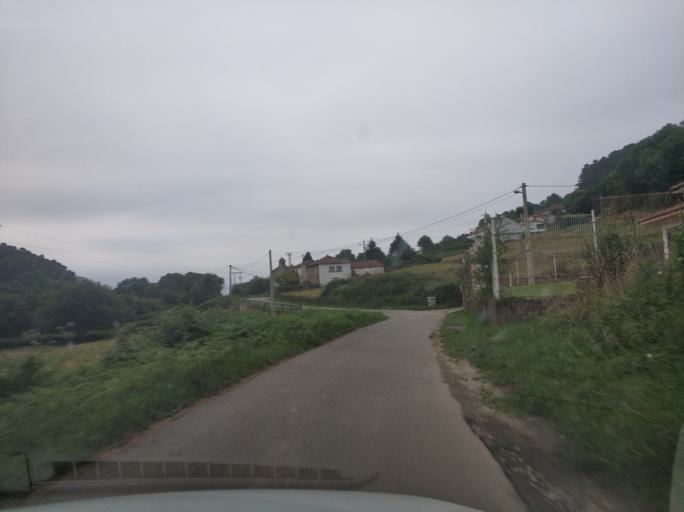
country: ES
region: Asturias
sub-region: Province of Asturias
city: Cudillero
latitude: 43.5581
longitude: -6.1886
